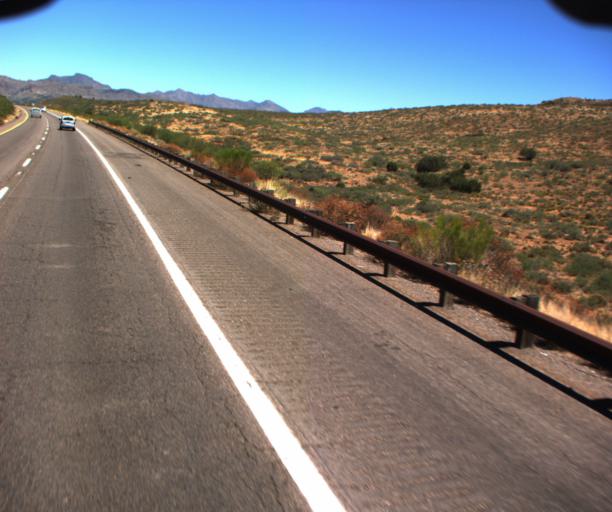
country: US
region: Arizona
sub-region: Gila County
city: Tonto Basin
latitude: 33.8521
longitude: -111.4700
